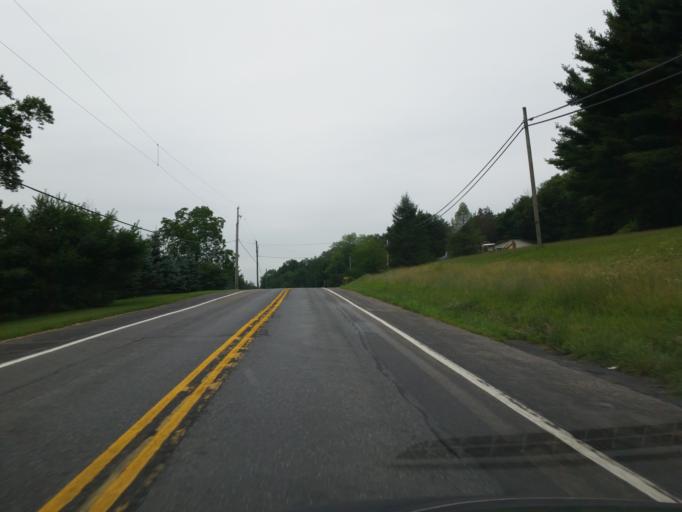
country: US
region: Pennsylvania
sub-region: Schuylkill County
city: Pine Grove
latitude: 40.5317
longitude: -76.4451
